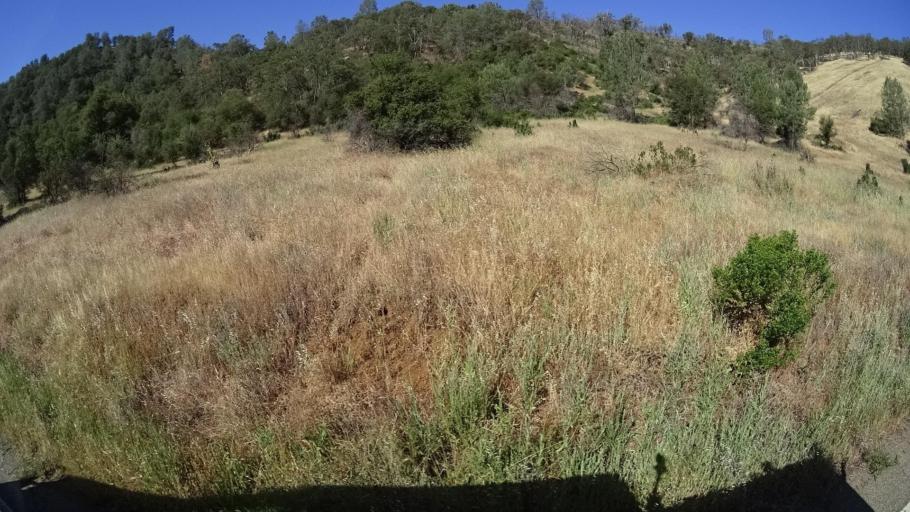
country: US
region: California
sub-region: Lake County
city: Clearlake Oaks
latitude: 38.9824
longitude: -122.6756
